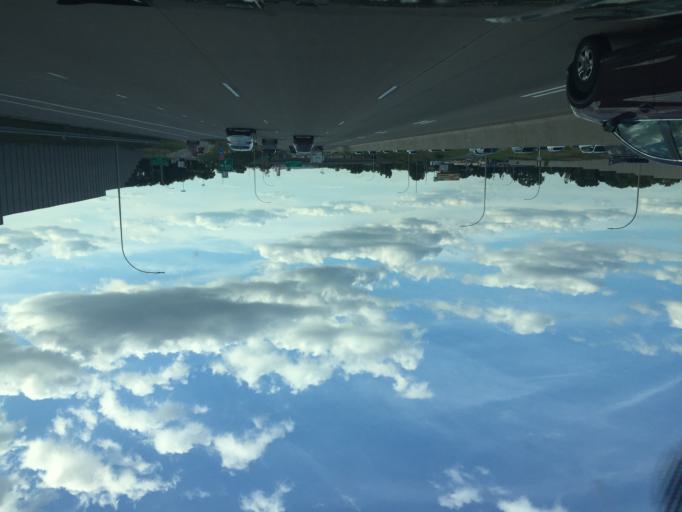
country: US
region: Minnesota
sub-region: Ramsey County
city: Little Canada
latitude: 44.9946
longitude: -93.0896
